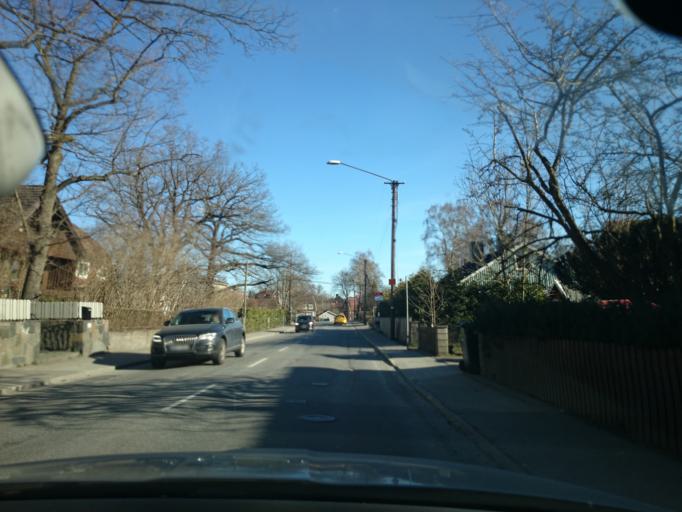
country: SE
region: Stockholm
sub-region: Huddinge Kommun
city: Huddinge
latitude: 59.2785
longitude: 17.9991
